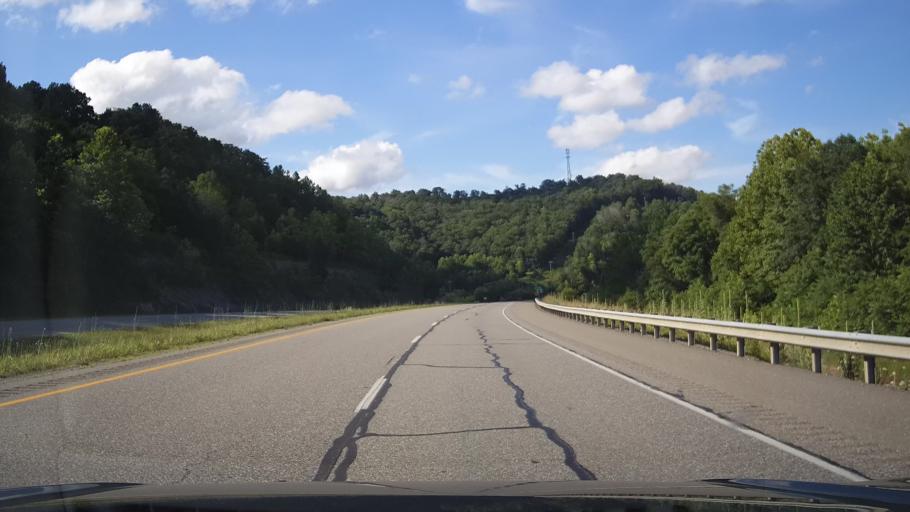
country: US
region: Kentucky
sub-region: Lawrence County
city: Louisa
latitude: 38.1656
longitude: -82.6454
